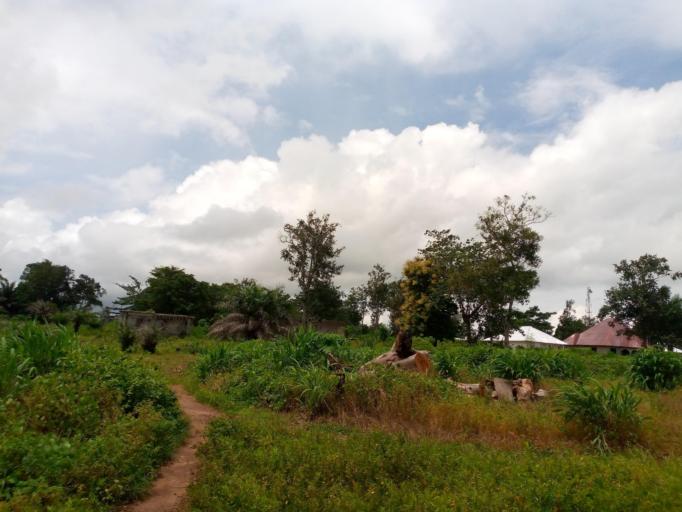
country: SL
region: Northern Province
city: Magburaka
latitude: 8.7268
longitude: -11.9345
